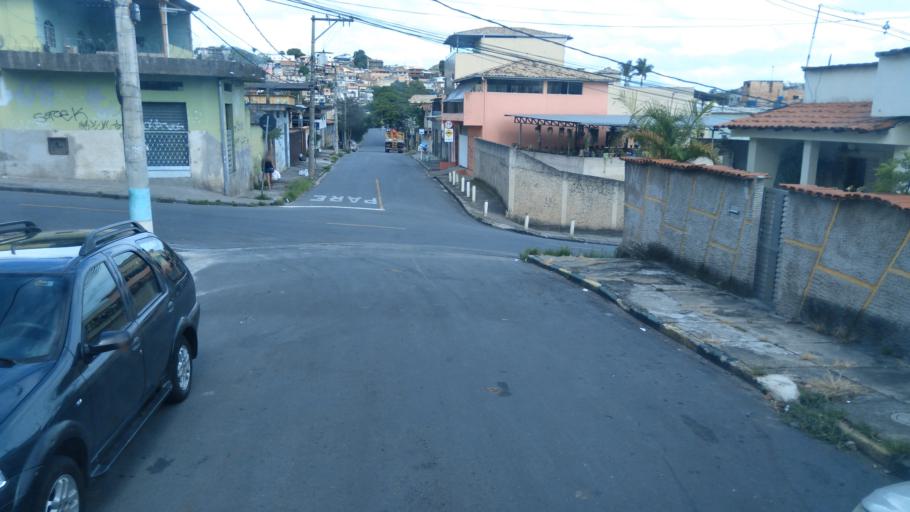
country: BR
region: Minas Gerais
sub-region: Belo Horizonte
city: Belo Horizonte
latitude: -19.8518
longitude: -43.9057
